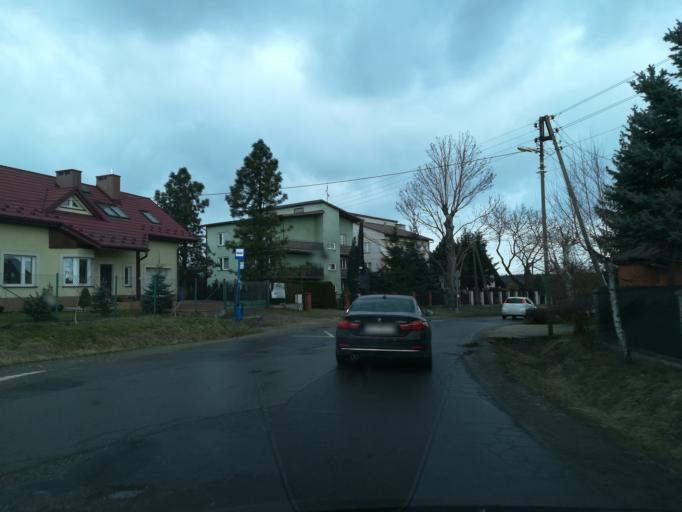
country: PL
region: Lesser Poland Voivodeship
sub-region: Krakow
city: Sidzina
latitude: 49.9901
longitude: 19.8597
